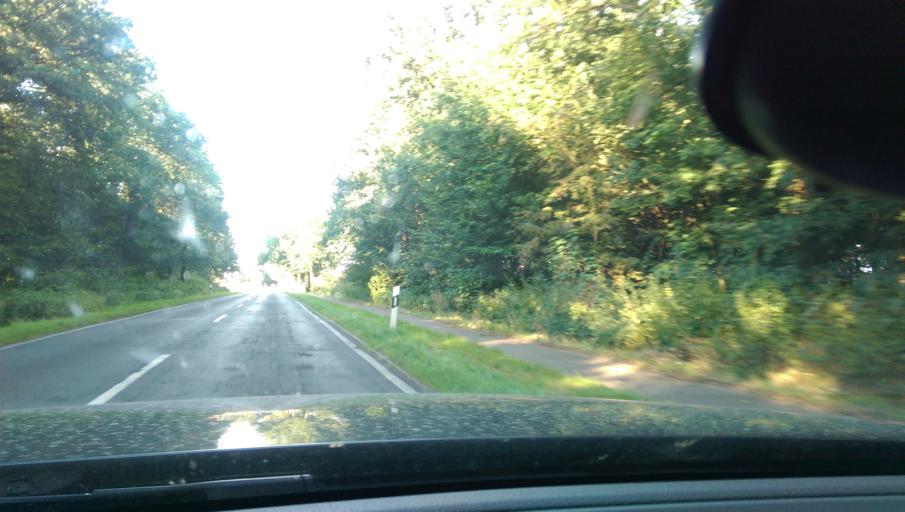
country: DE
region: Lower Saxony
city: Schwarmstedt
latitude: 52.5897
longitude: 9.5906
